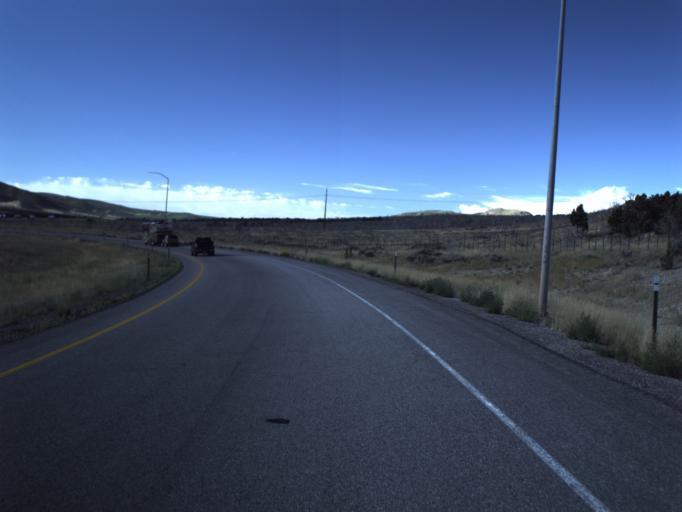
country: US
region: Utah
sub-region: Beaver County
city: Beaver
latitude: 38.5745
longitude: -112.6068
